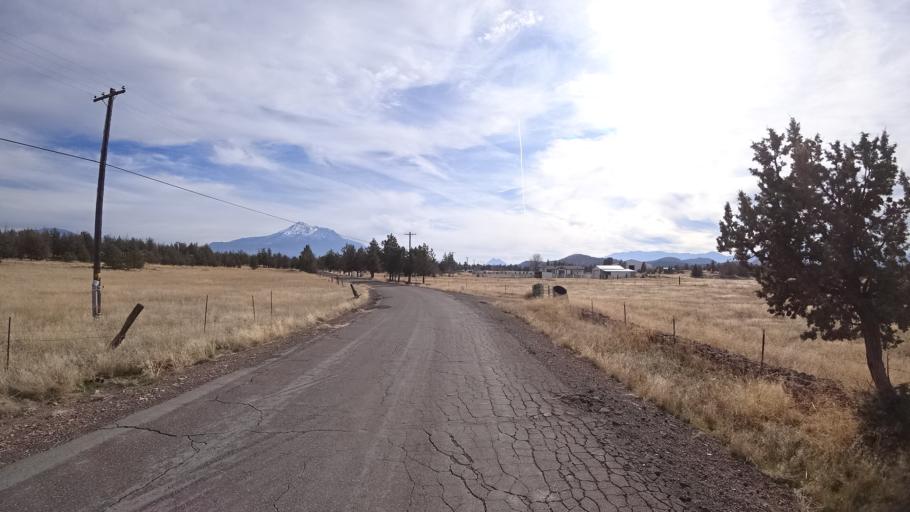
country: US
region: California
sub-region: Siskiyou County
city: Weed
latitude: 41.5943
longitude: -122.4029
